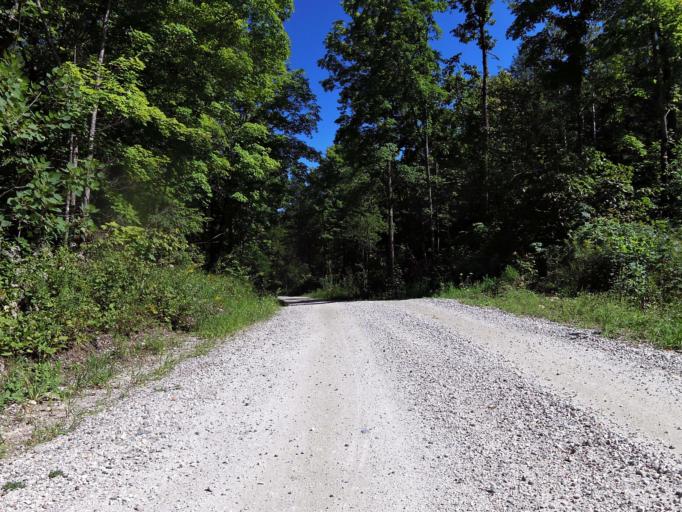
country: CA
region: Ontario
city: Renfrew
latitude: 45.1346
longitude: -76.7010
